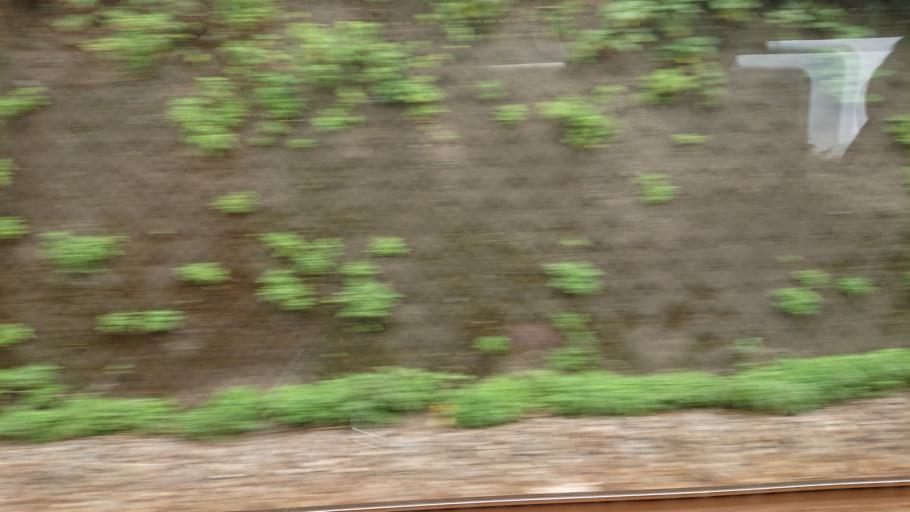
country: TW
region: Taiwan
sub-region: Yilan
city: Yilan
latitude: 24.9114
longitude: 121.8764
